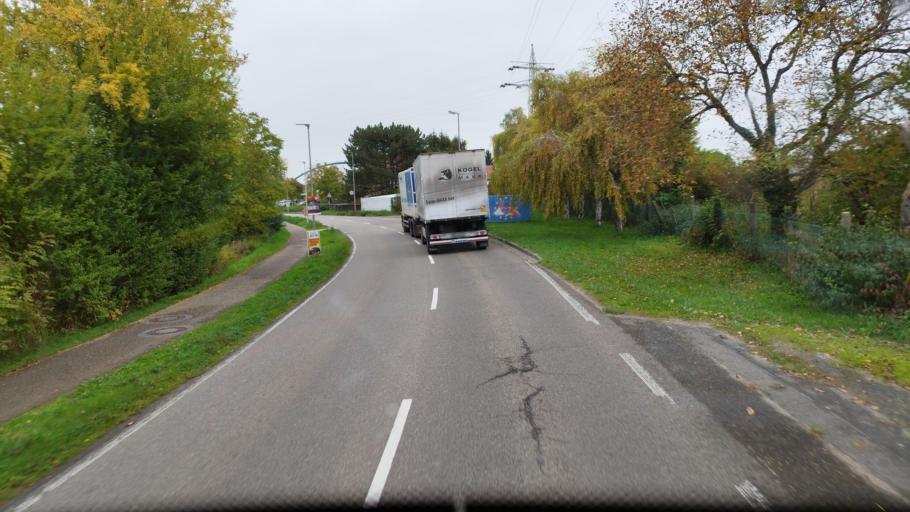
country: DE
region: Rheinland-Pfalz
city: Worth am Rhein
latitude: 49.0459
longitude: 8.2640
